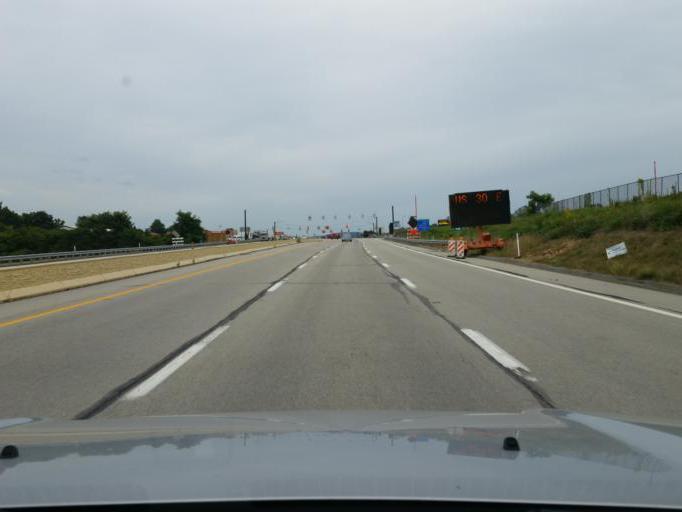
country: US
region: Pennsylvania
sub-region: Westmoreland County
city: Lawson Heights
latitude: 40.2839
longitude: -79.3979
